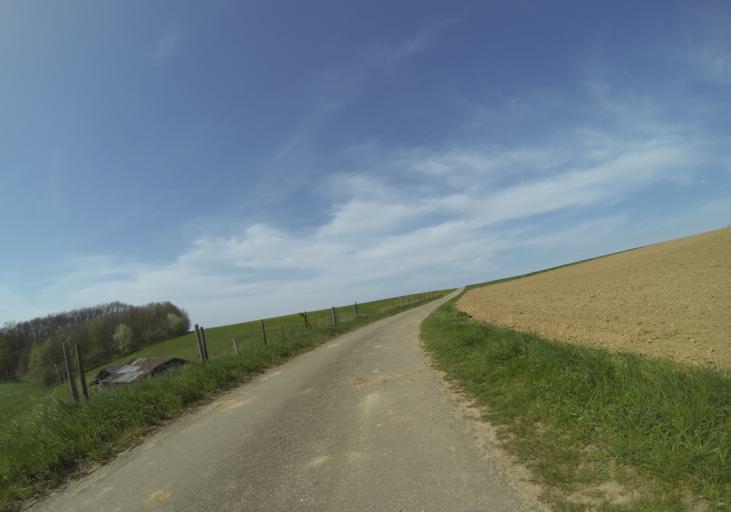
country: DE
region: Baden-Wuerttemberg
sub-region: Tuebingen Region
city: Burgrieden
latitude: 48.2539
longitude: 9.9285
